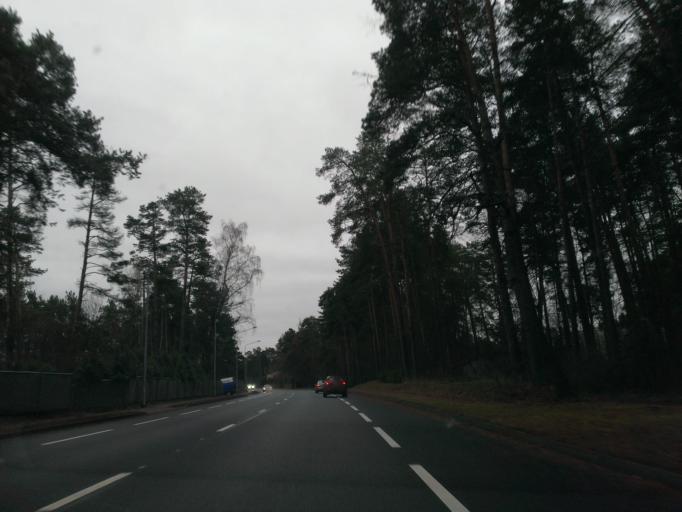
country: LV
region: Adazi
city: Adazi
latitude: 57.0396
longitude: 24.3154
